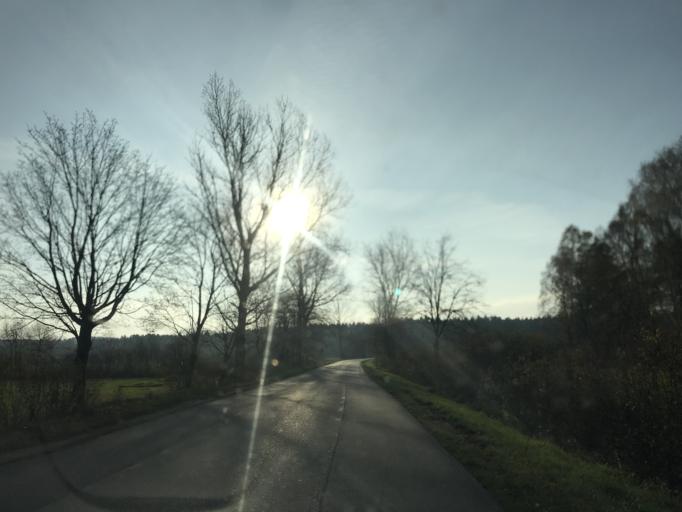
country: PL
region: Pomeranian Voivodeship
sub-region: Powiat pucki
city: Krokowa
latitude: 54.8075
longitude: 18.0980
